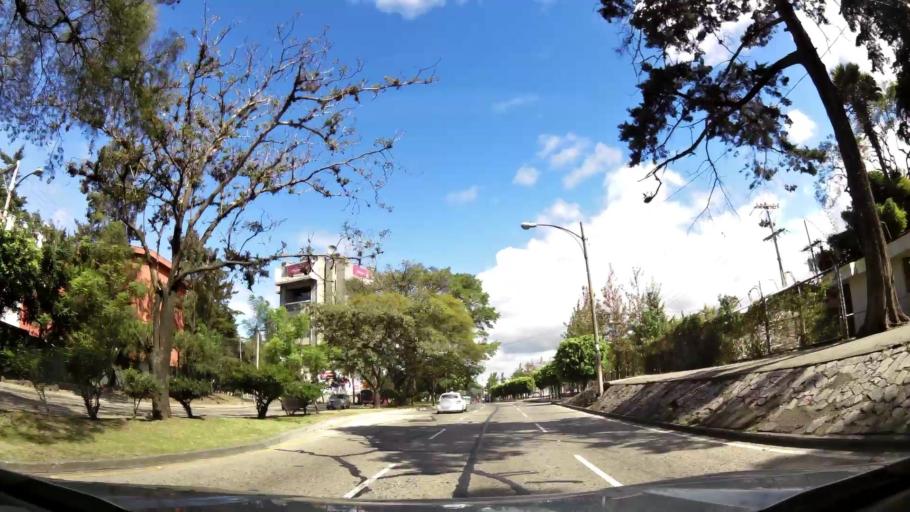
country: GT
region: Guatemala
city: Guatemala City
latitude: 14.6088
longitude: -90.5261
